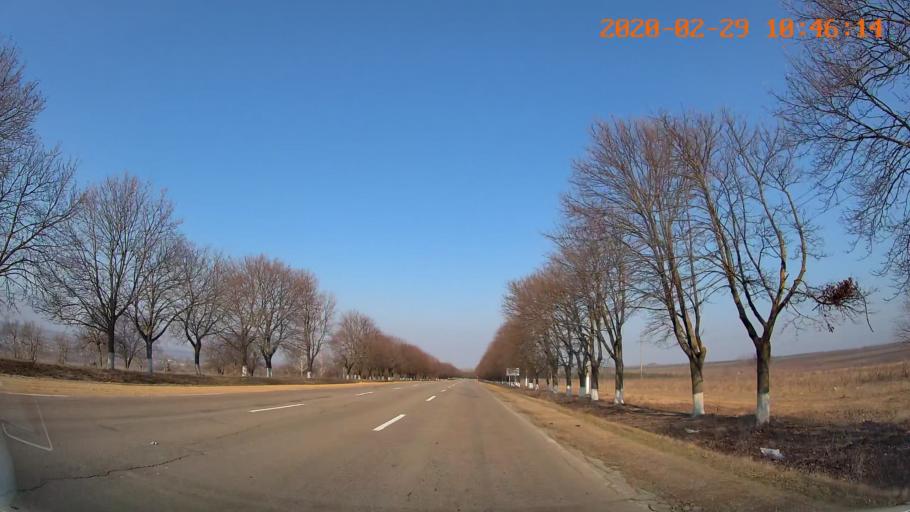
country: MD
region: Telenesti
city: Grigoriopol
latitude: 47.0825
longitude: 29.3757
